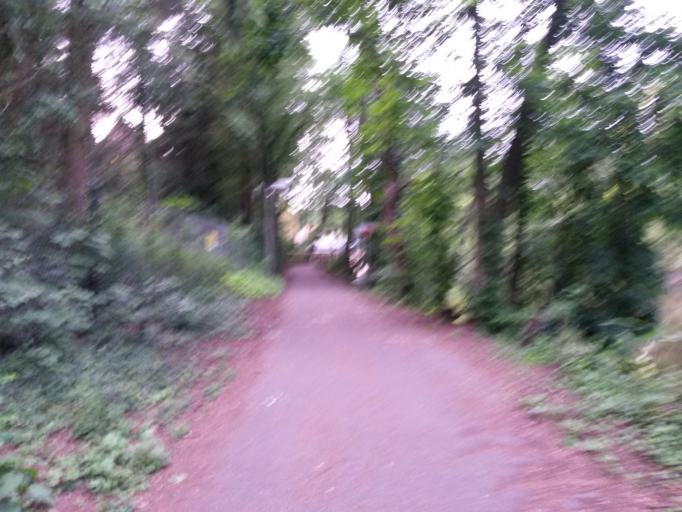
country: DE
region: Bavaria
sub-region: Regierungsbezirk Mittelfranken
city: Stein
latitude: 49.4141
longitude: 11.0191
